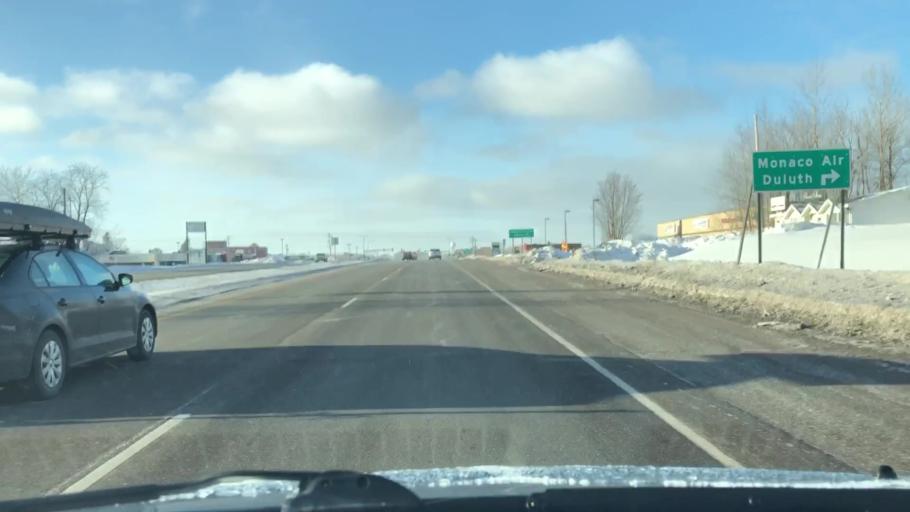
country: US
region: Minnesota
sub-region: Saint Louis County
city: Hermantown
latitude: 46.8254
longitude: -92.1919
